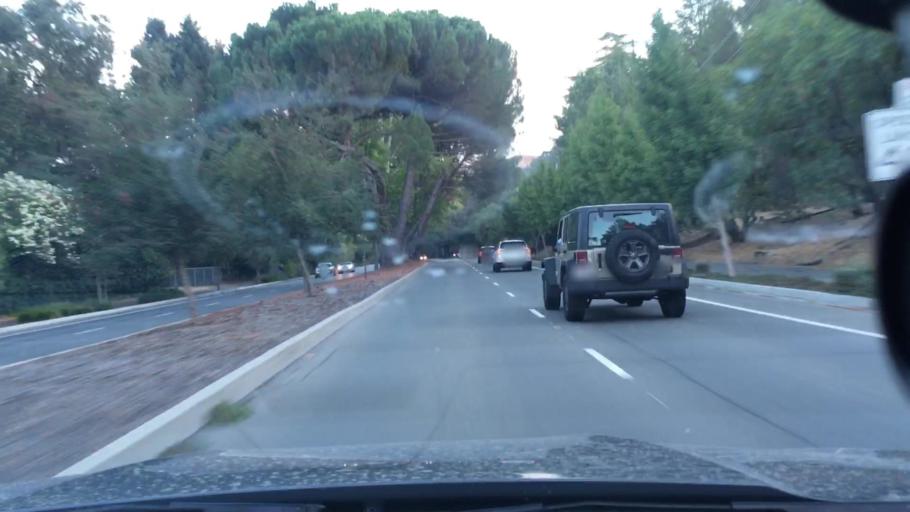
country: US
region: California
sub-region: Contra Costa County
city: Saranap
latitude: 37.8908
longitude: -122.0940
